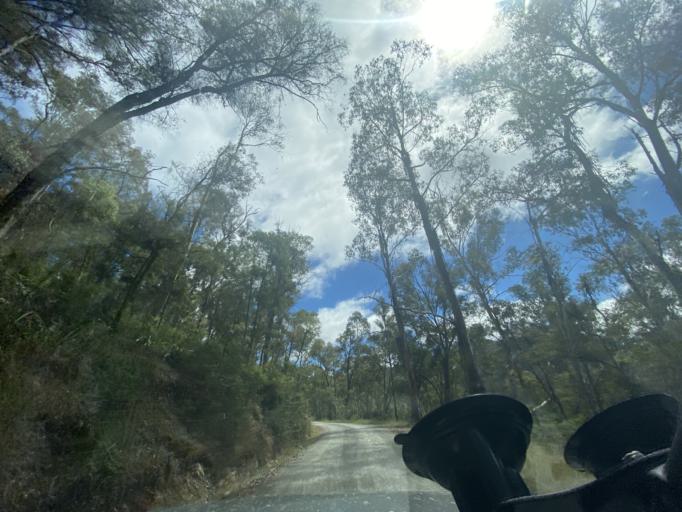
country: AU
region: Victoria
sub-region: Yarra Ranges
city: Millgrove
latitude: -37.5224
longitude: 146.0459
